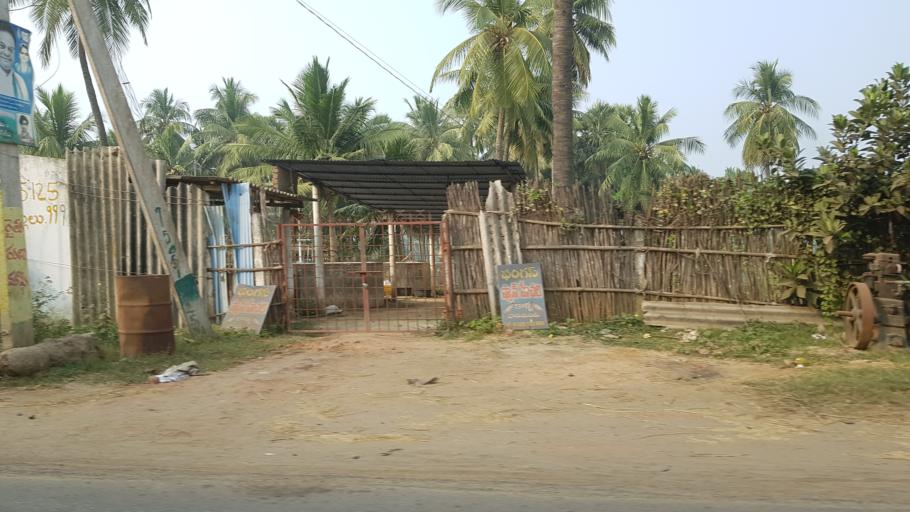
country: IN
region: Andhra Pradesh
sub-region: West Godavari
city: Akividu
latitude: 16.5378
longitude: 81.4169
